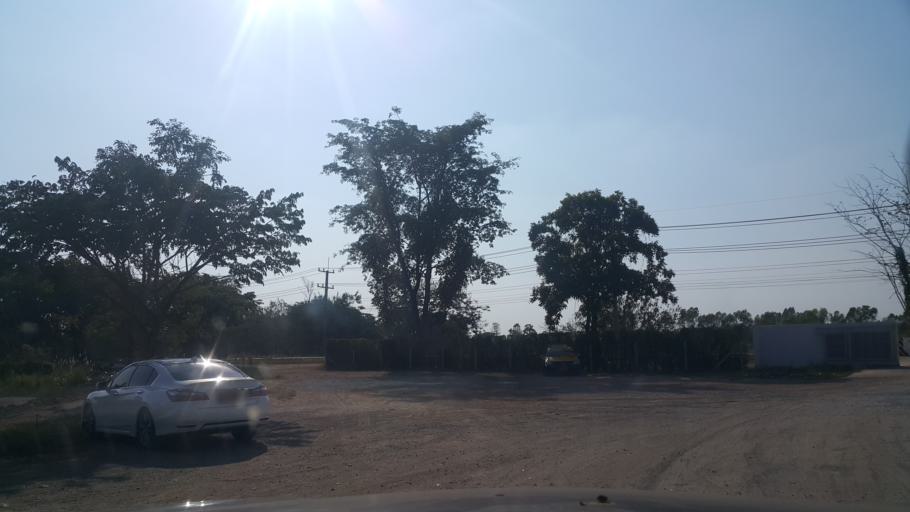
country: TH
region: Khon Kaen
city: Khon Kaen
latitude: 16.4105
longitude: 102.8828
